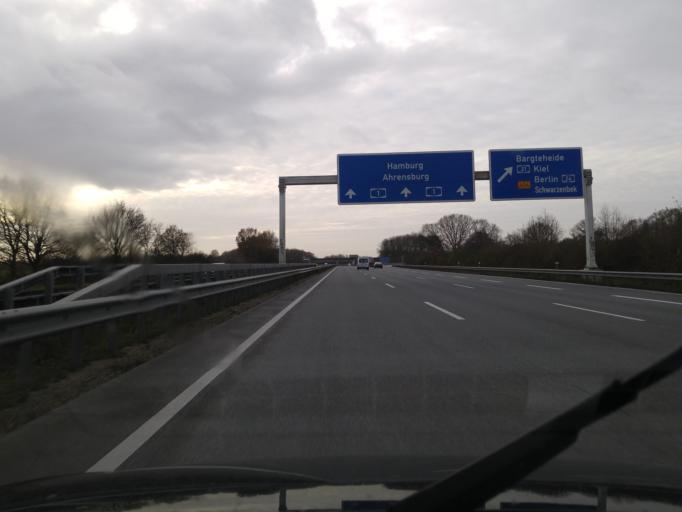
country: DE
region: Schleswig-Holstein
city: Hammoor
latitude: 53.7227
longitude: 10.3423
